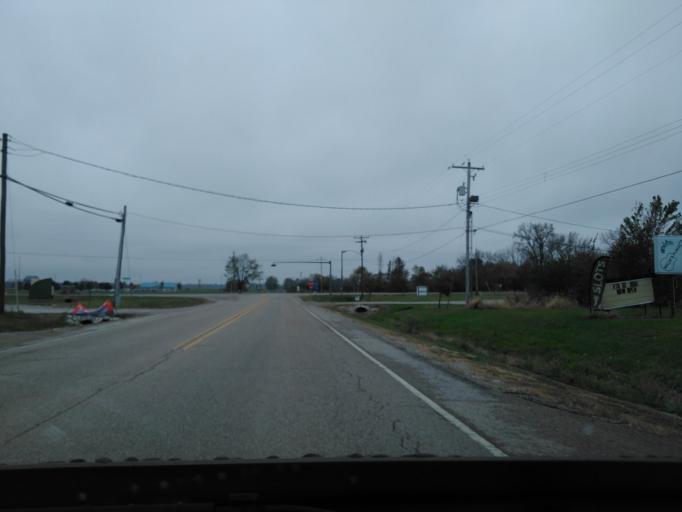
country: US
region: Illinois
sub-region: Bond County
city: Greenville
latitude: 38.8707
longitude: -89.4142
